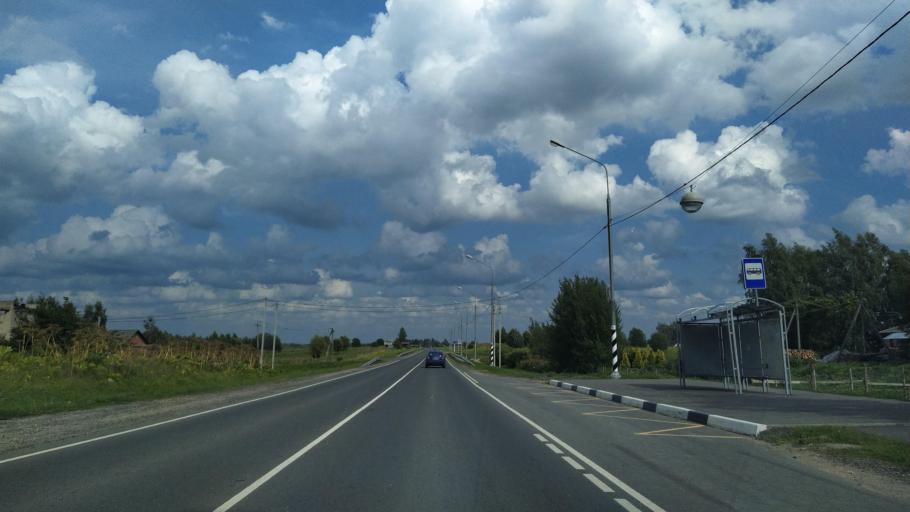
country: RU
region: Novgorod
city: Sol'tsy
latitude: 58.0831
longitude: 30.1133
